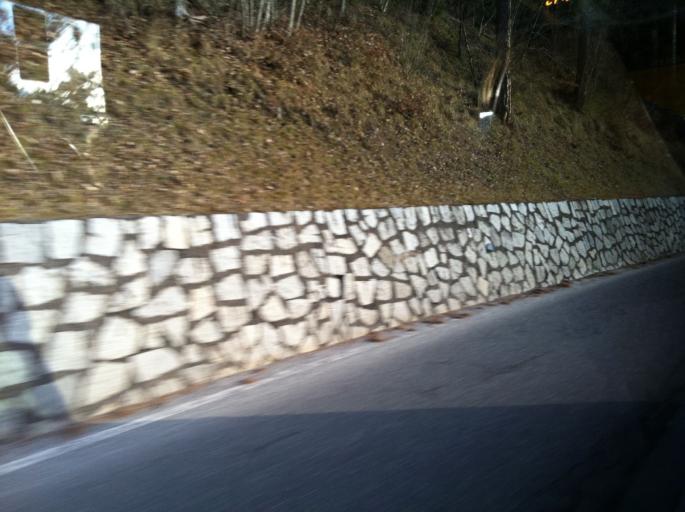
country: IT
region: Trentino-Alto Adige
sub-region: Bolzano
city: Bressanone
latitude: 46.6989
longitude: 11.6626
